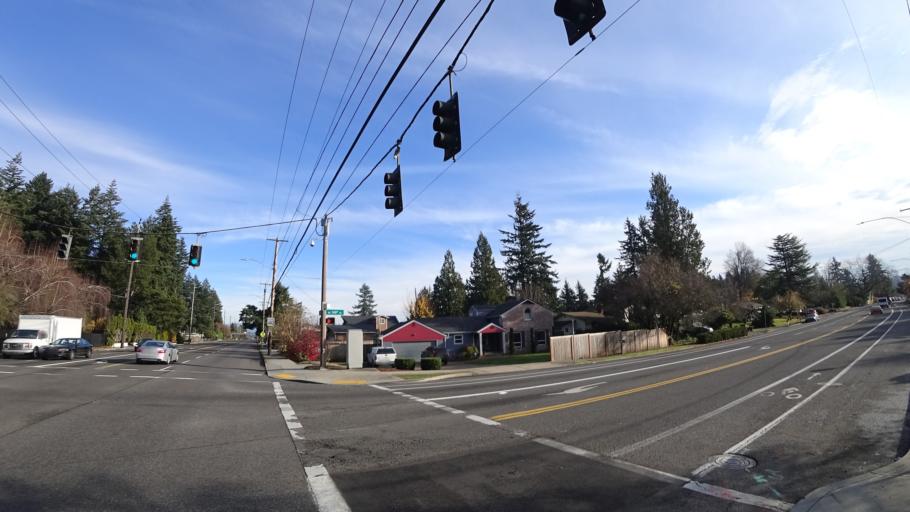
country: US
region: Oregon
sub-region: Multnomah County
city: Lents
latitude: 45.5264
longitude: -122.5107
